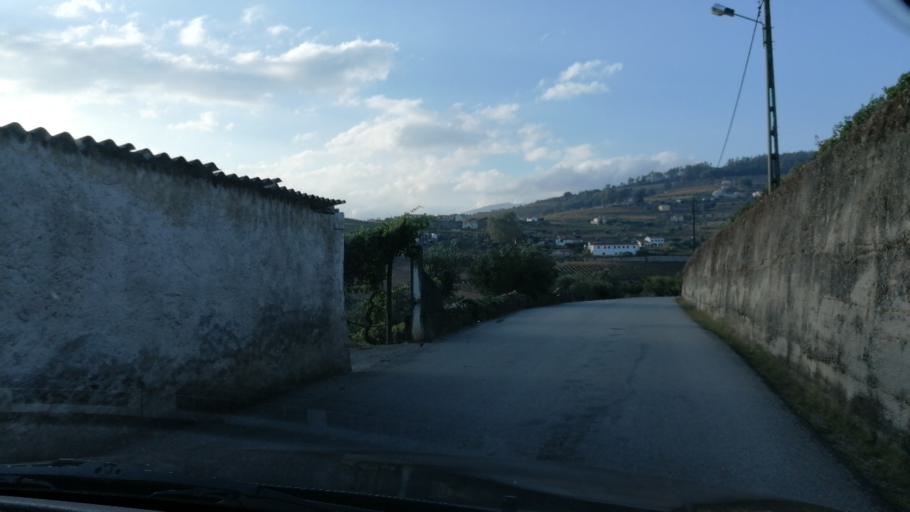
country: PT
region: Vila Real
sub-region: Peso da Regua
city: Godim
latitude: 41.1569
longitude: -7.8172
